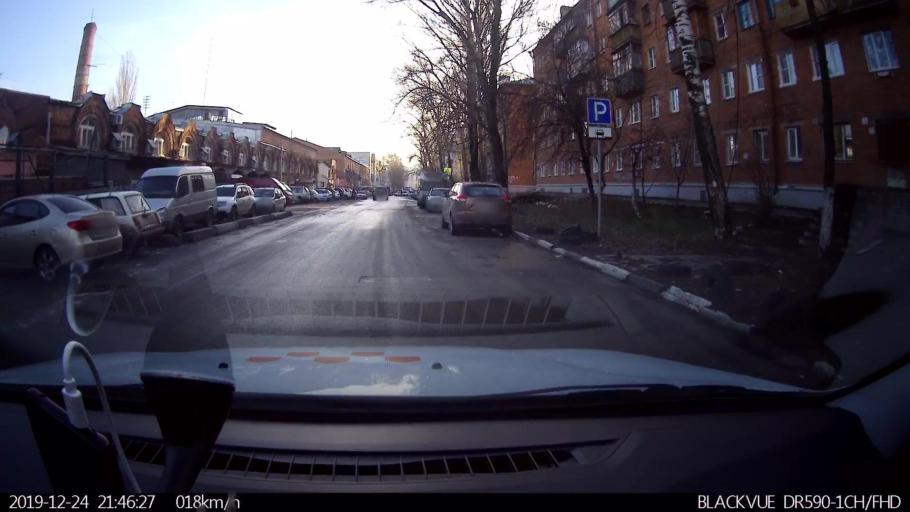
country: RU
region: Nizjnij Novgorod
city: Nizhniy Novgorod
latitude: 56.3321
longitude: 43.9569
